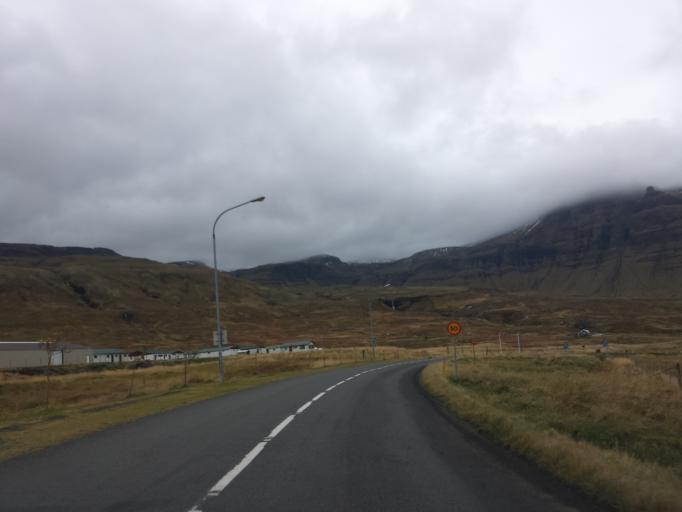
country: IS
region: West
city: Olafsvik
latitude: 64.9227
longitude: -23.2767
